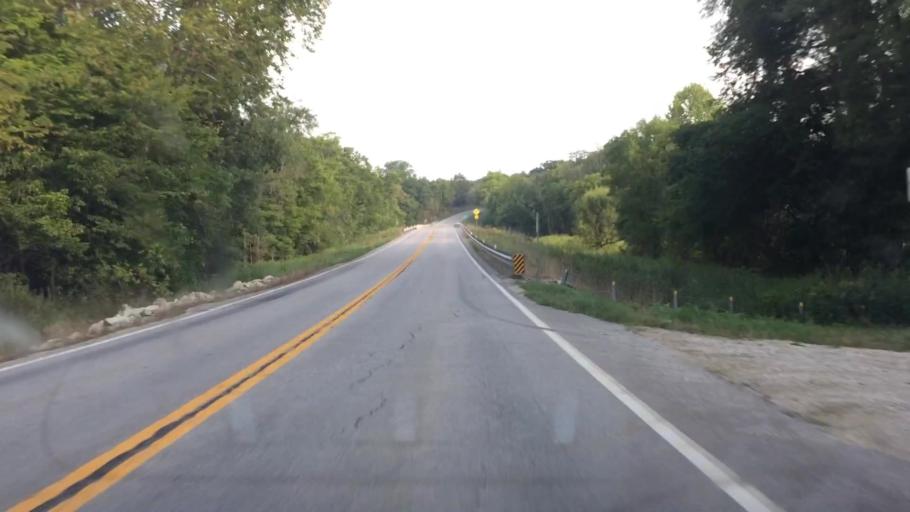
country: US
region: Missouri
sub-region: Greene County
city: Strafford
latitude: 37.1905
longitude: -93.1264
